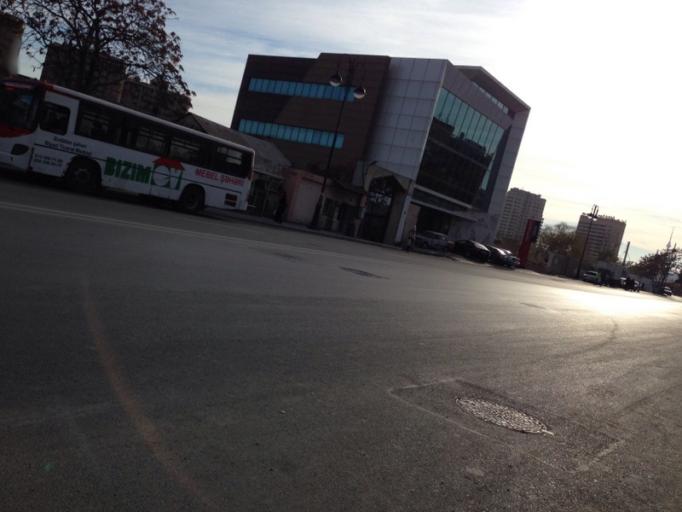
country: AZ
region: Baki
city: Baku
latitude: 40.3840
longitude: 49.8529
